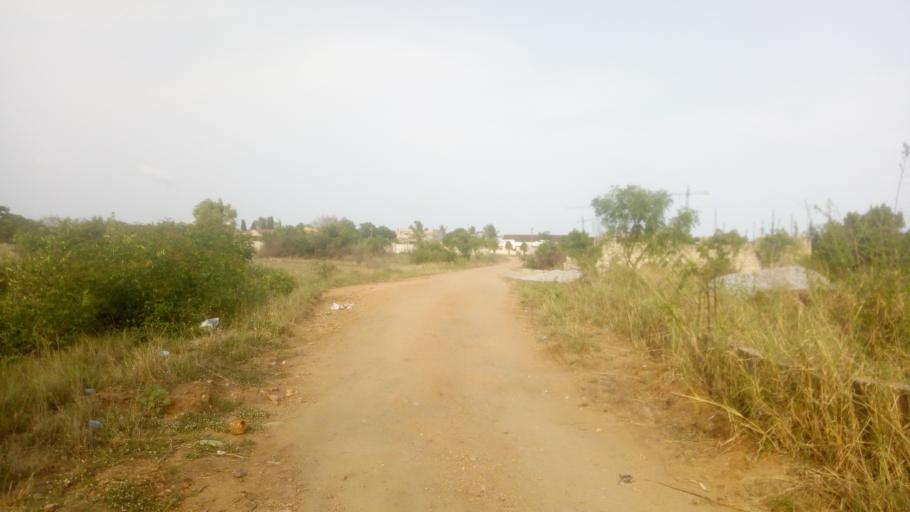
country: GH
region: Central
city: Winneba
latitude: 5.3771
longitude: -0.6302
